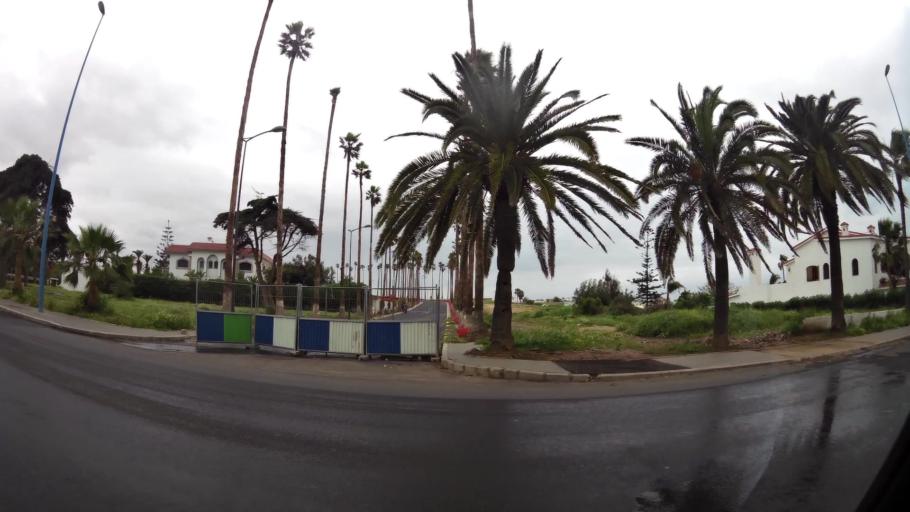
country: MA
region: Grand Casablanca
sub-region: Casablanca
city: Casablanca
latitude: 33.5991
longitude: -7.6601
